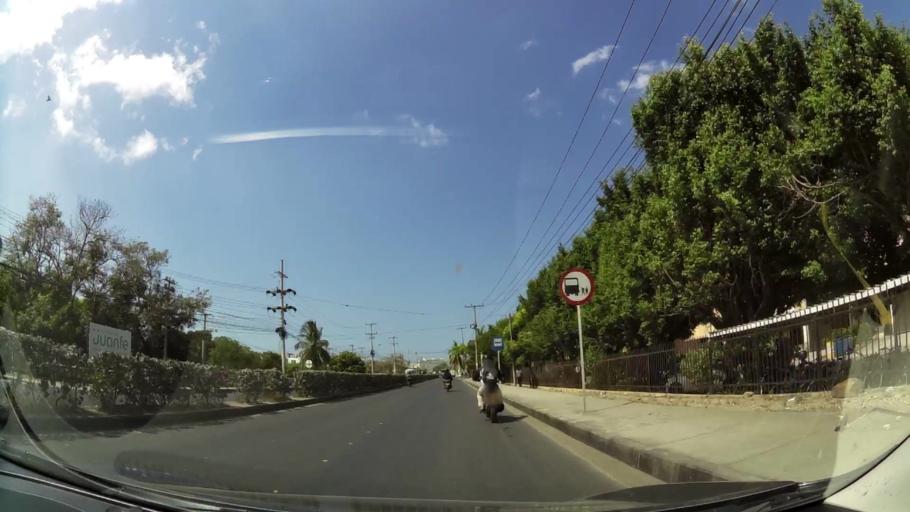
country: CO
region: Bolivar
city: Cartagena
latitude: 10.3790
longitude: -75.4626
